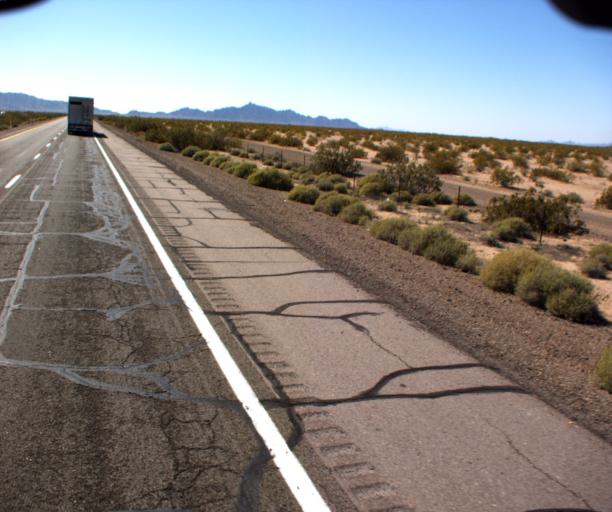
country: US
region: Arizona
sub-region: Yuma County
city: Wellton
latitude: 32.7727
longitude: -113.6047
